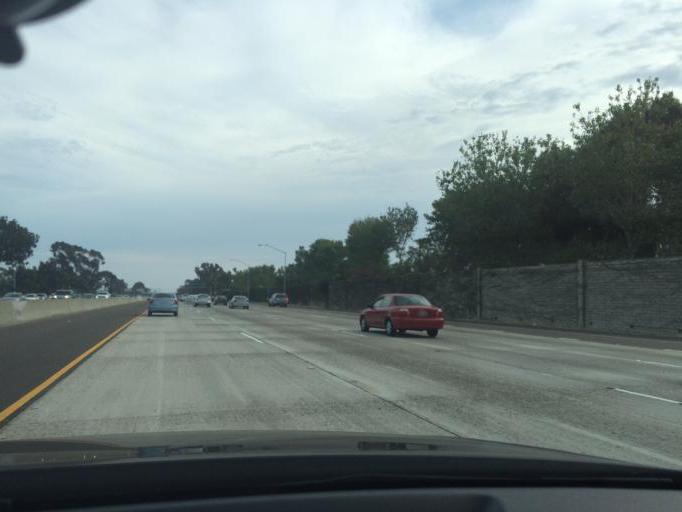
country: US
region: California
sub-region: San Diego County
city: San Diego
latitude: 32.7967
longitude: -117.1573
